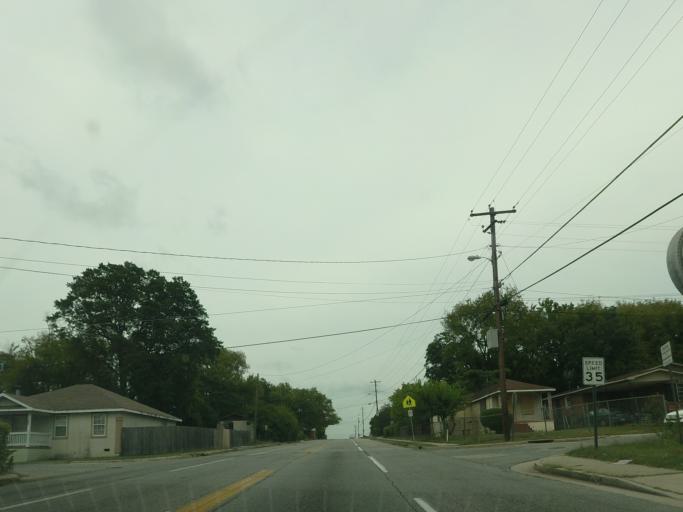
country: US
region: Georgia
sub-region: Bibb County
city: Macon
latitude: 32.8202
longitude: -83.6619
